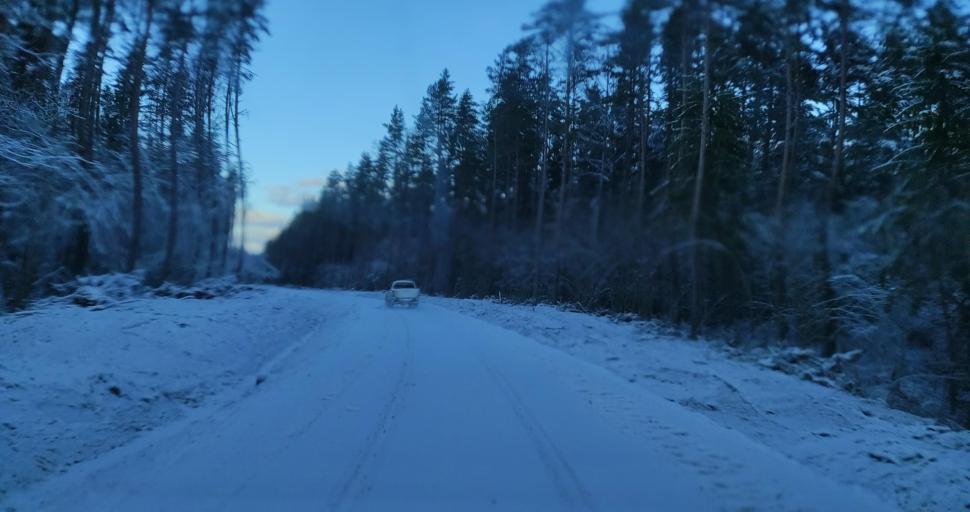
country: LV
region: Skrunda
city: Skrunda
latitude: 56.5903
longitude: 21.9526
